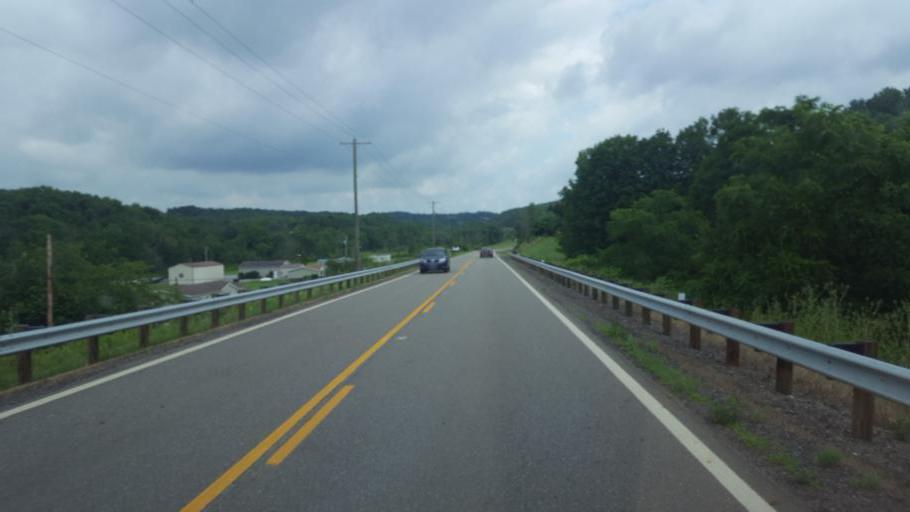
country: US
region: Ohio
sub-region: Columbiana County
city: Lisbon
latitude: 40.7313
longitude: -80.7898
